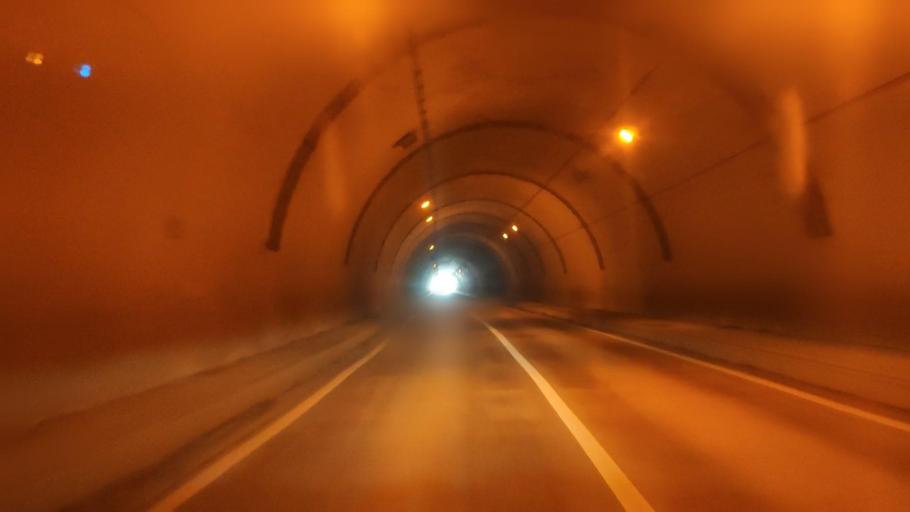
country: JP
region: Kumamoto
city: Hitoyoshi
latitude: 32.3825
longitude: 130.8353
